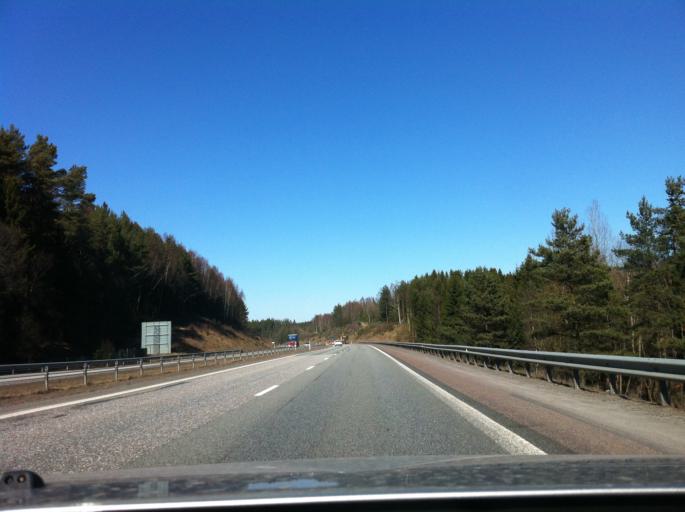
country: SE
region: Joenkoeping
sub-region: Jonkopings Kommun
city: Odensjo
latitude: 57.7146
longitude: 14.1603
